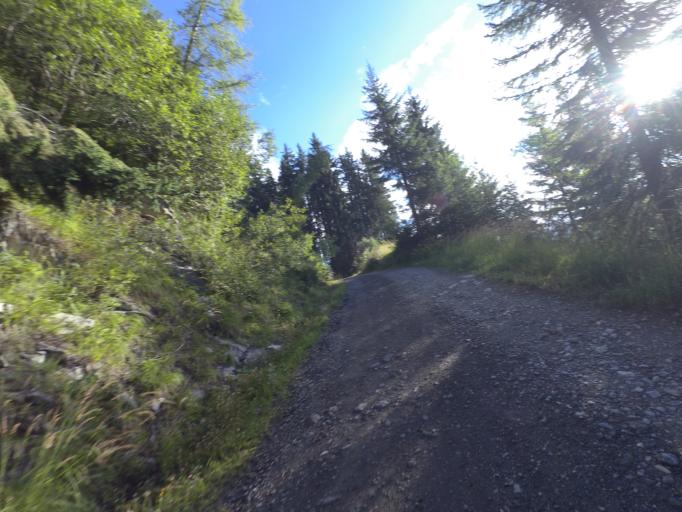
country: AT
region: Salzburg
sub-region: Politischer Bezirk Sankt Johann im Pongau
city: Muhlbach am Hochkonig
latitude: 47.3525
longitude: 13.1037
